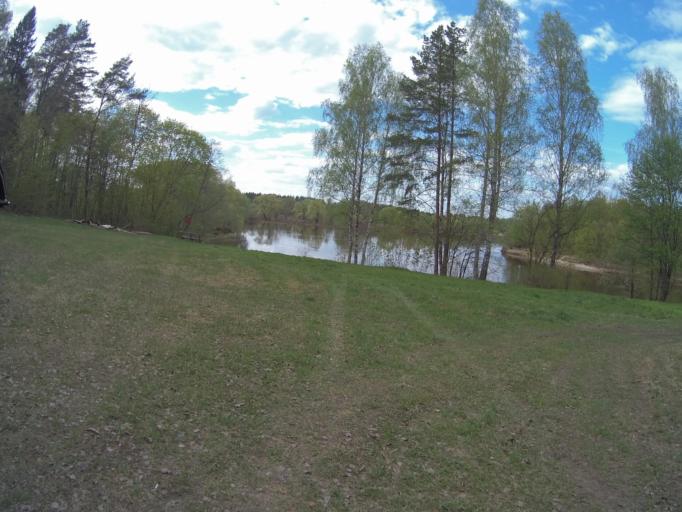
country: RU
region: Vladimir
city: Orgtrud
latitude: 56.1227
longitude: 40.7017
